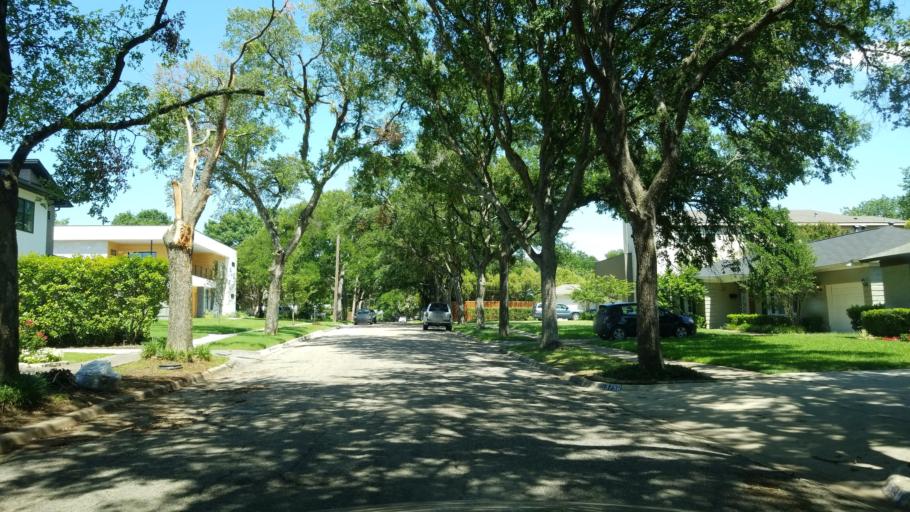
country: US
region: Texas
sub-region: Dallas County
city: University Park
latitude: 32.8776
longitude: -96.8539
